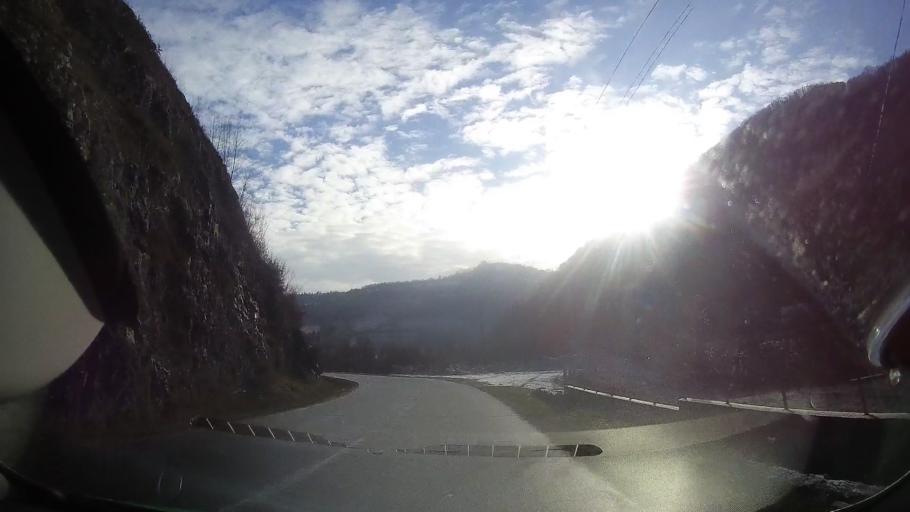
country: RO
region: Alba
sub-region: Comuna Sohodol
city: Sohodol
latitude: 46.3586
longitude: 23.0232
